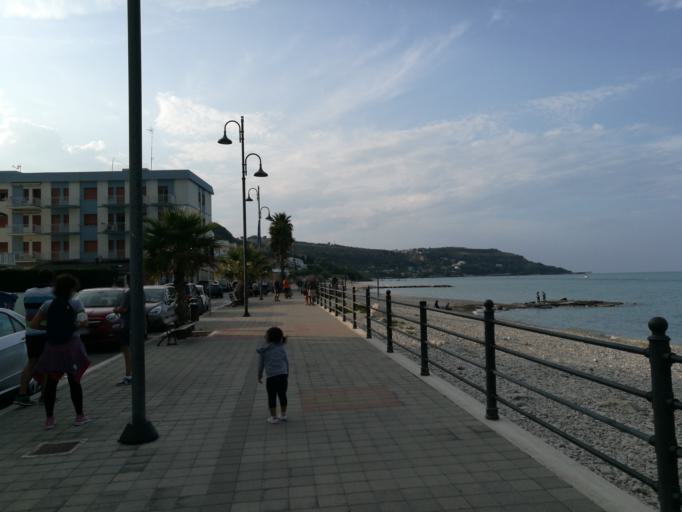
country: IT
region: Abruzzo
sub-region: Provincia di Chieti
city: Fossacesia
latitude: 42.2515
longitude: 14.5094
